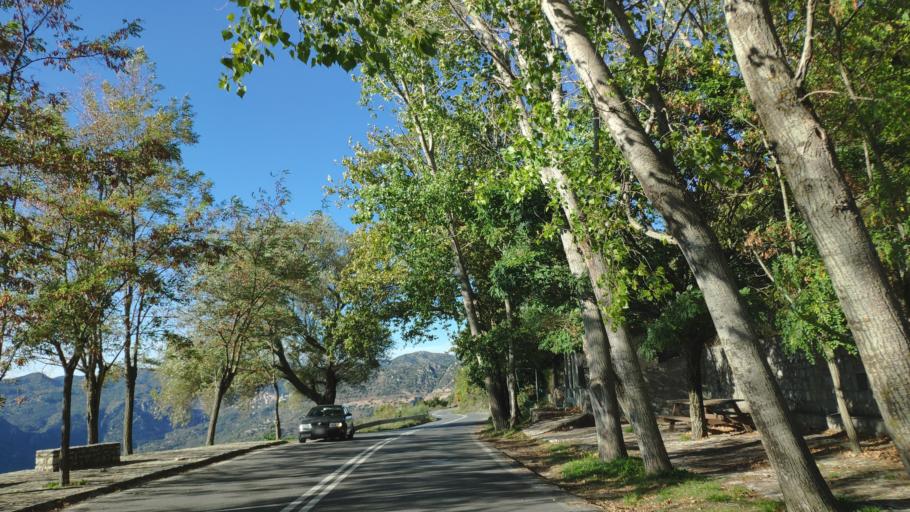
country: GR
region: Peloponnese
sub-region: Nomos Arkadias
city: Dimitsana
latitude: 37.5600
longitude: 22.0629
